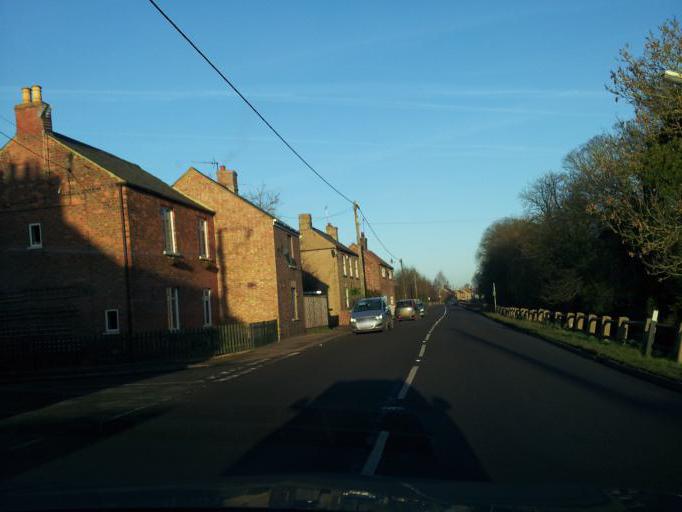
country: GB
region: England
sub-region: Norfolk
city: Outwell
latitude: 52.6030
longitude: 0.2225
